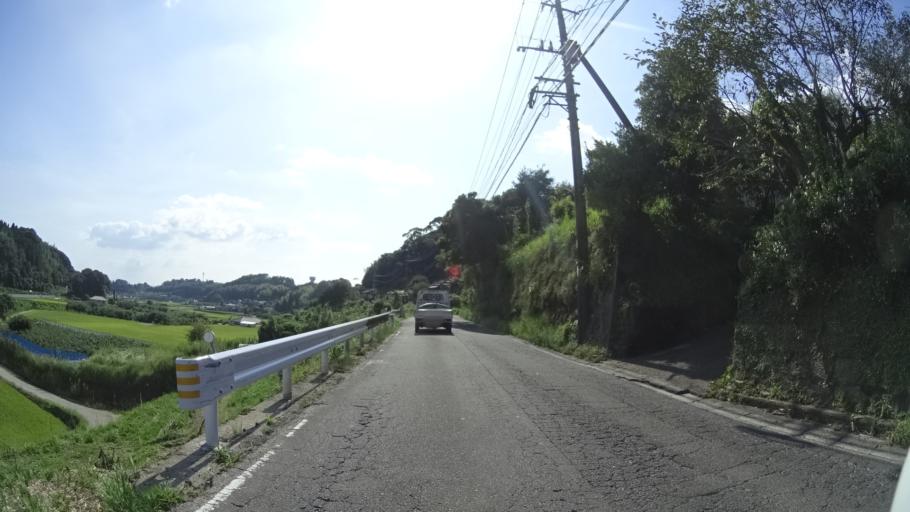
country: JP
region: Kagoshima
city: Kagoshima-shi
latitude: 31.6647
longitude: 130.5553
